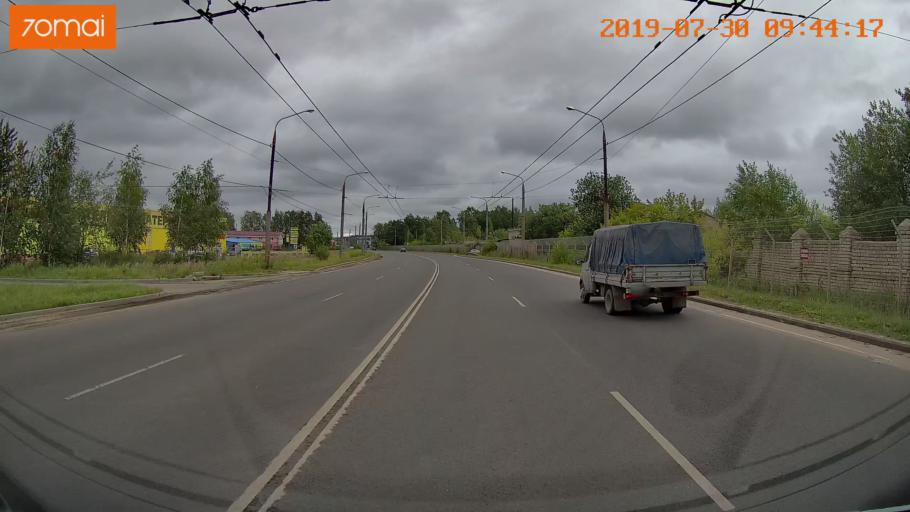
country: RU
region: Ivanovo
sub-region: Gorod Ivanovo
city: Ivanovo
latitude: 56.9487
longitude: 40.9613
